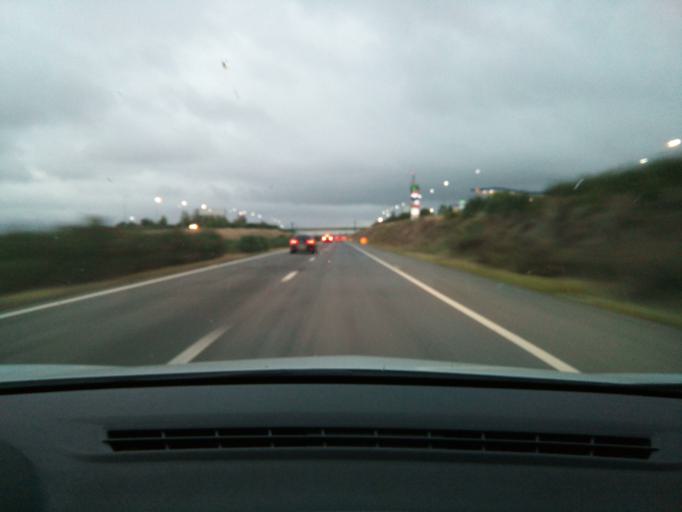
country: MA
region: Meknes-Tafilalet
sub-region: Meknes
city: Meknes
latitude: 33.8327
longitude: -5.5735
